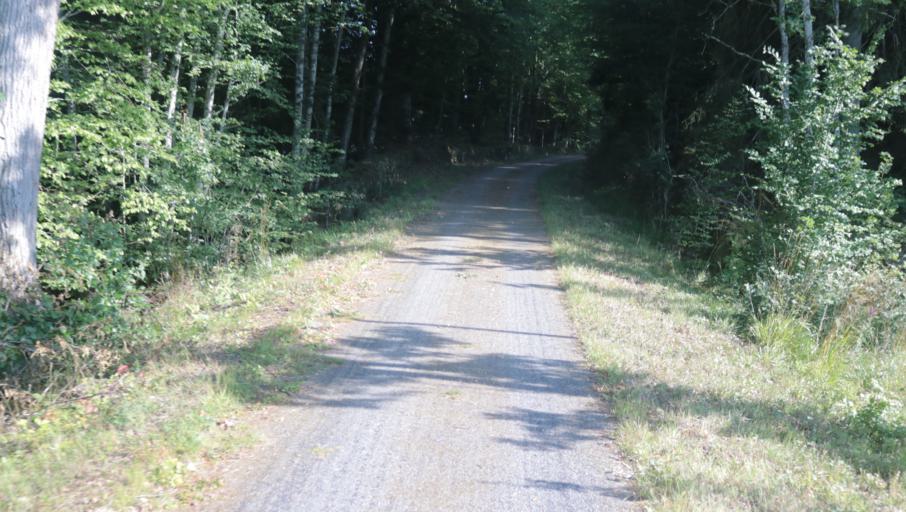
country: SE
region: Blekinge
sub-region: Karlshamns Kommun
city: Svangsta
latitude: 56.3798
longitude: 14.6788
